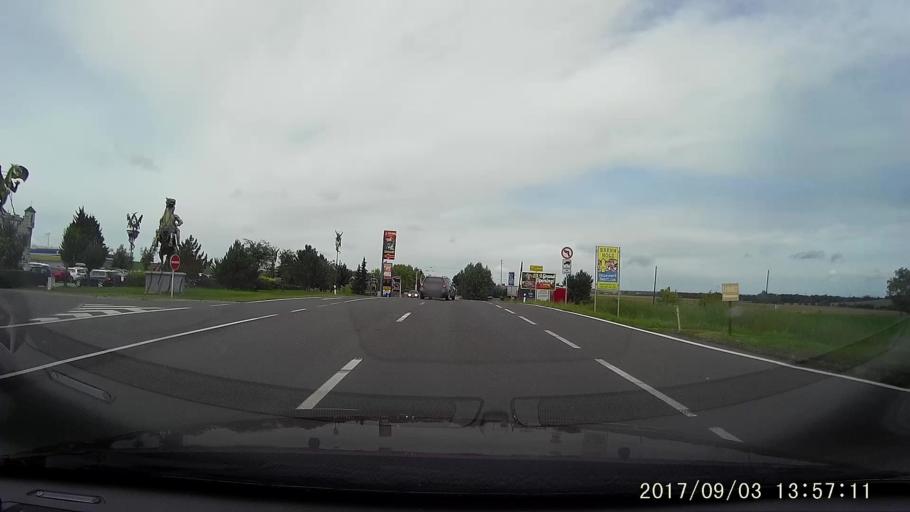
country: CZ
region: South Moravian
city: Vrbovec
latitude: 48.7651
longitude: 16.0668
